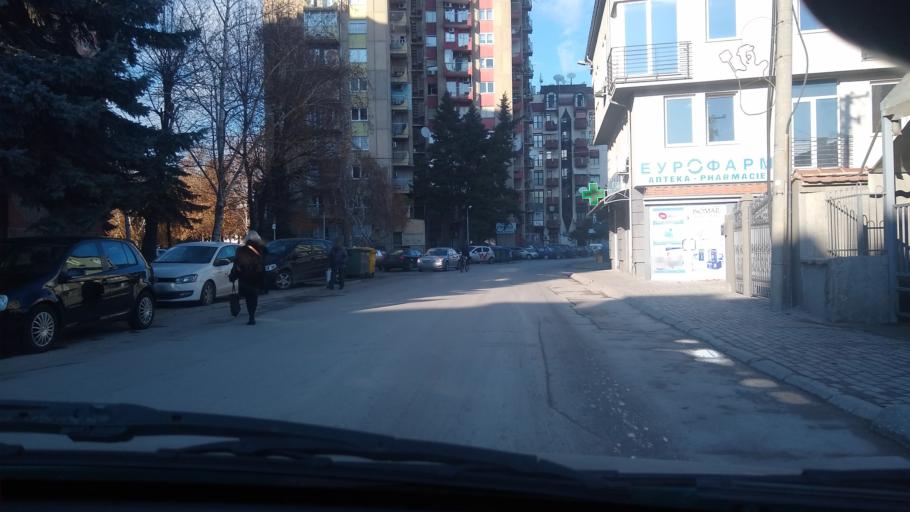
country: MK
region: Bitola
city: Bitola
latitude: 41.0258
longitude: 21.3335
